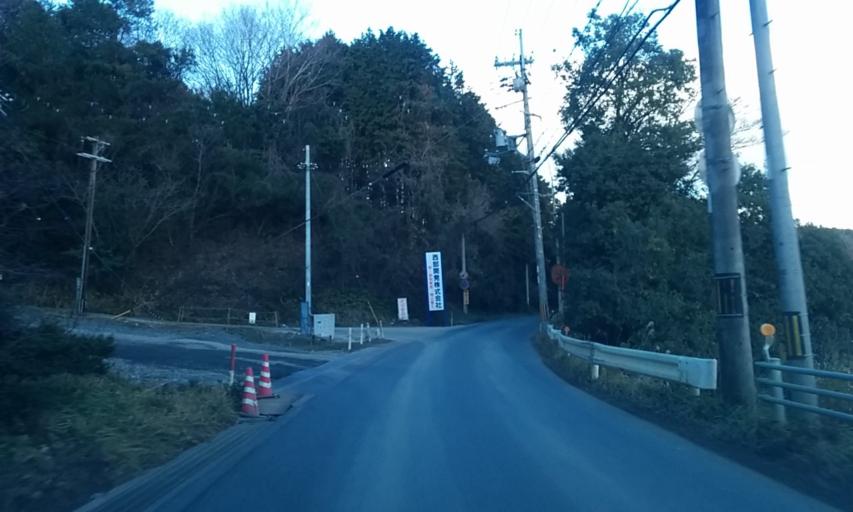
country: JP
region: Kyoto
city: Fukuchiyama
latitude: 35.3072
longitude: 135.1469
